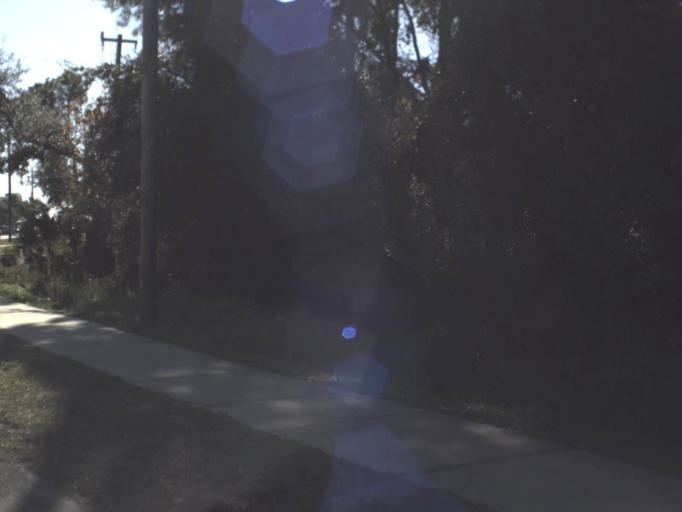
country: US
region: Florida
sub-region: Volusia County
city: Holly Hill
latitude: 29.2145
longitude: -81.0630
